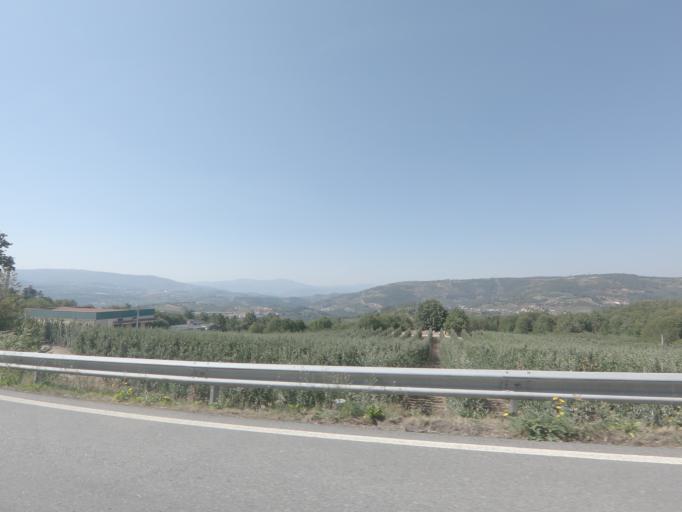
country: PT
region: Viseu
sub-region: Tarouca
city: Tarouca
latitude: 41.0390
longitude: -7.7348
